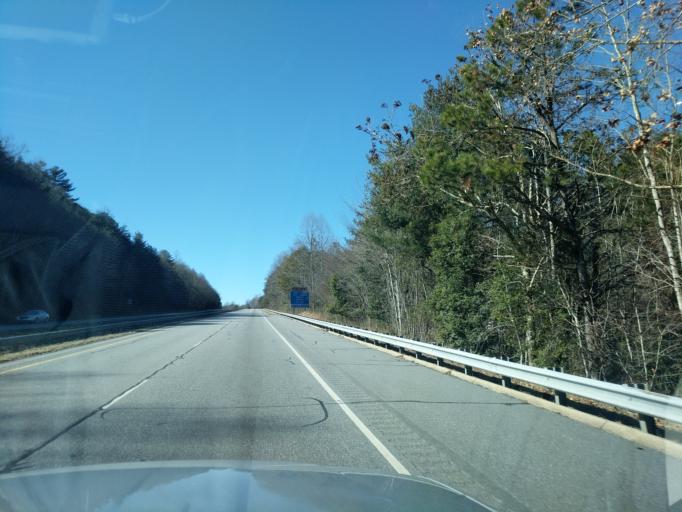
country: US
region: North Carolina
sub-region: Swain County
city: Bryson City
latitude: 35.4250
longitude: -83.4257
